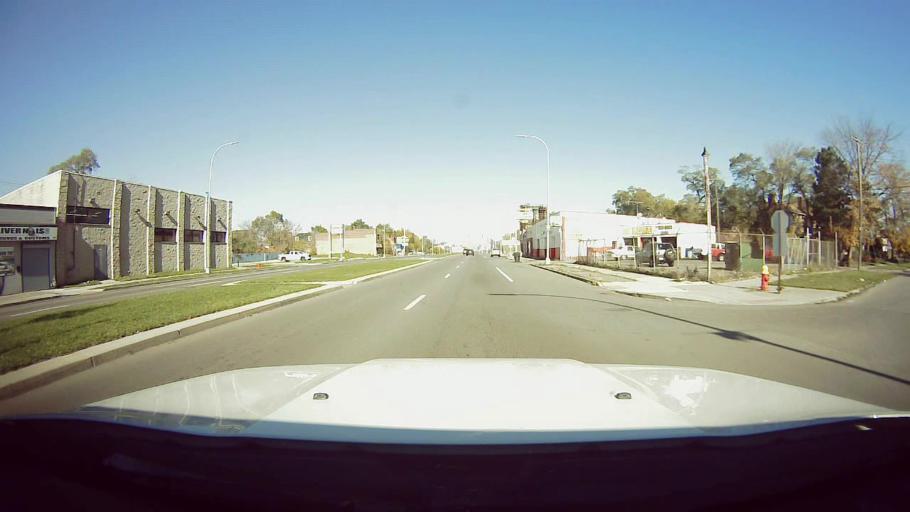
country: US
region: Michigan
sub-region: Wayne County
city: Highland Park
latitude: 42.3798
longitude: -83.1391
